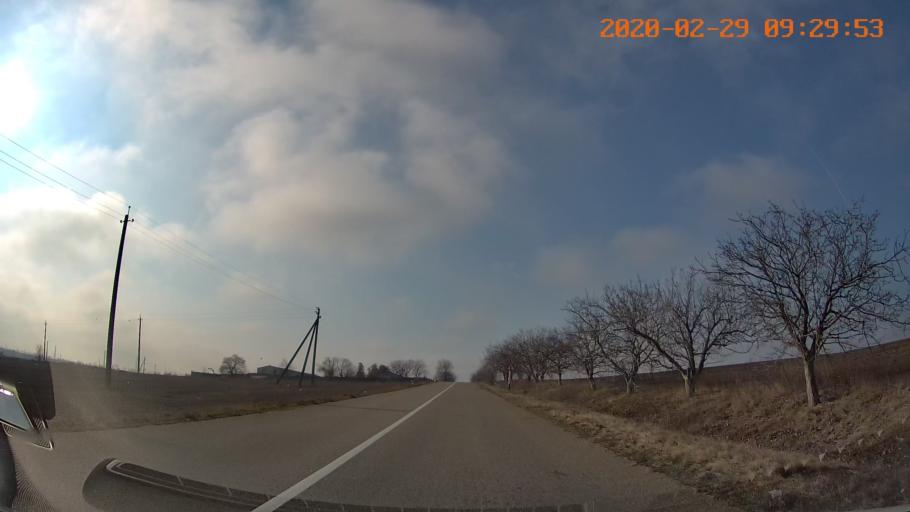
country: UA
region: Odessa
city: Lymanske
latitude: 46.6730
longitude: 29.9191
